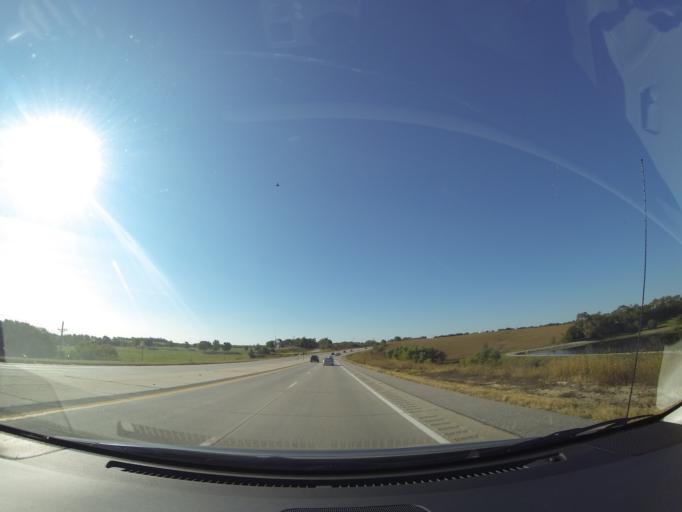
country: US
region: Nebraska
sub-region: Sarpy County
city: Gretna
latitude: 41.1593
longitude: -96.2343
